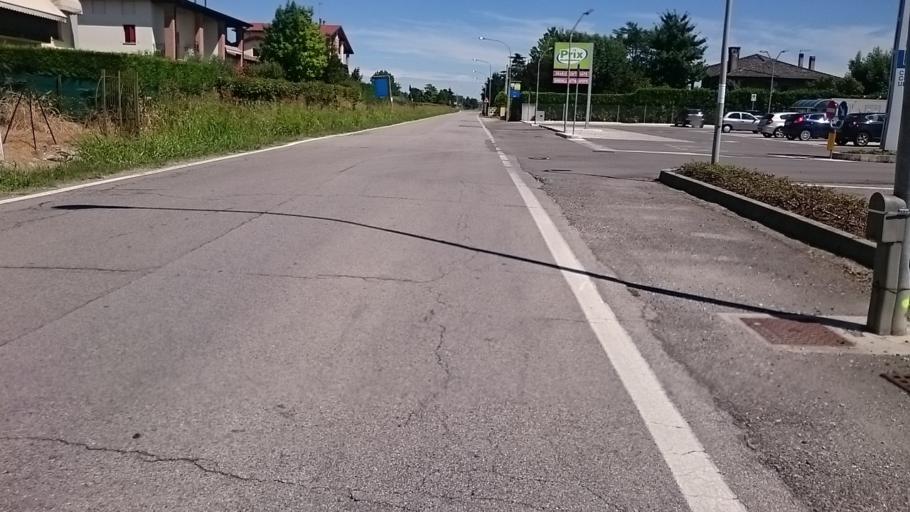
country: IT
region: Veneto
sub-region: Provincia di Venezia
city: Pianiga
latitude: 45.4534
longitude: 12.0266
